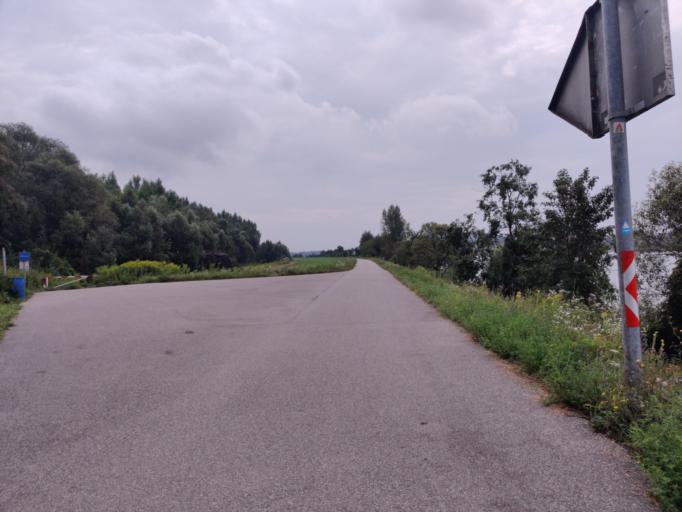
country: AT
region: Upper Austria
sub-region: Politischer Bezirk Urfahr-Umgebung
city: Steyregg
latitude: 48.2816
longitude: 14.3495
